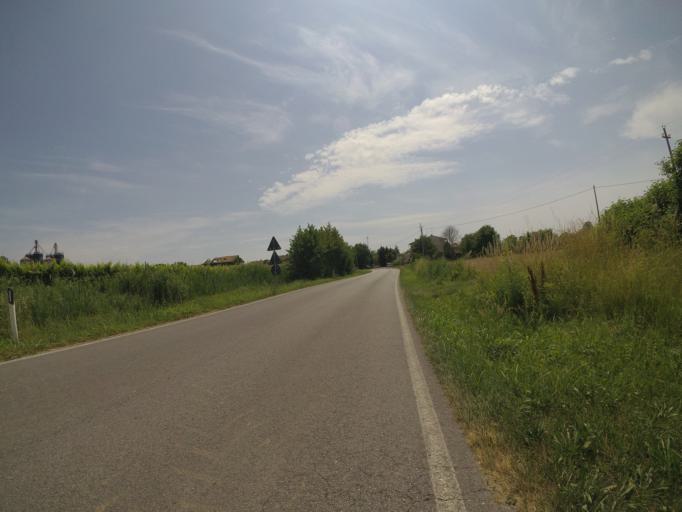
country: IT
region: Friuli Venezia Giulia
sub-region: Provincia di Udine
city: Teor
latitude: 45.8751
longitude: 13.0879
